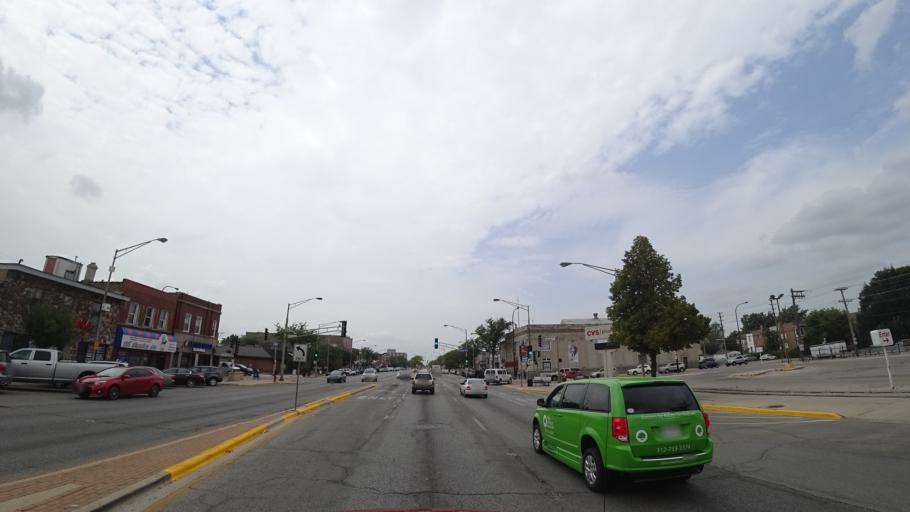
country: US
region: Illinois
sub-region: Cook County
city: Cicero
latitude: 41.8510
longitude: -87.7632
